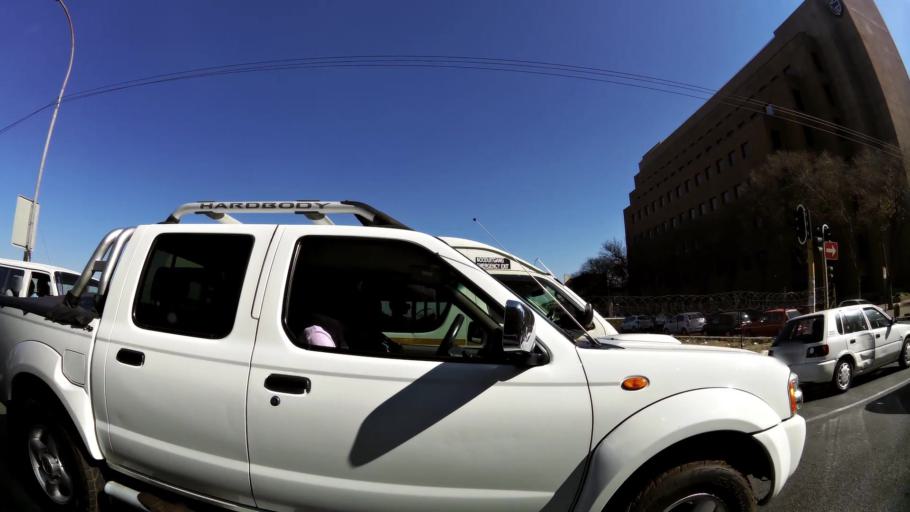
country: ZA
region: Gauteng
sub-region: City of Johannesburg Metropolitan Municipality
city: Johannesburg
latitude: -26.2100
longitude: 28.0386
